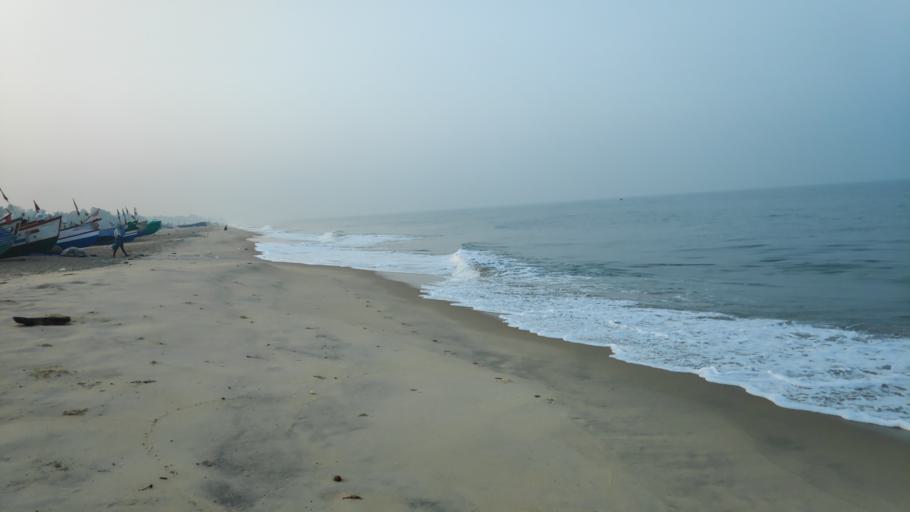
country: IN
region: Kerala
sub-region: Alappuzha
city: Vayalar
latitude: 9.6601
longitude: 76.2918
